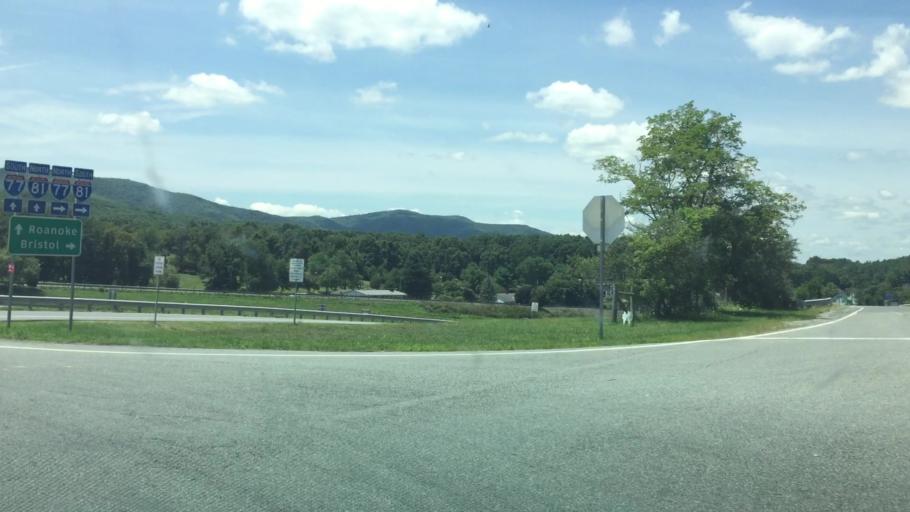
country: US
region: Virginia
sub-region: Wythe County
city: Wytheville
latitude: 36.9381
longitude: -80.9943
